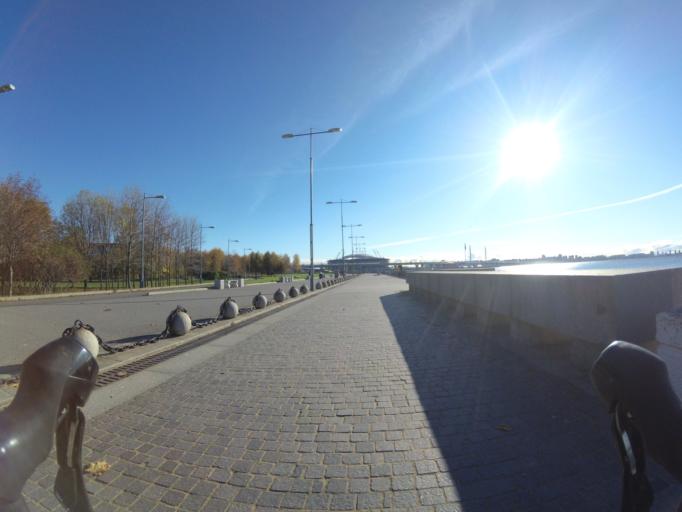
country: RU
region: Leningrad
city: Untolovo
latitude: 59.9809
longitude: 30.2025
